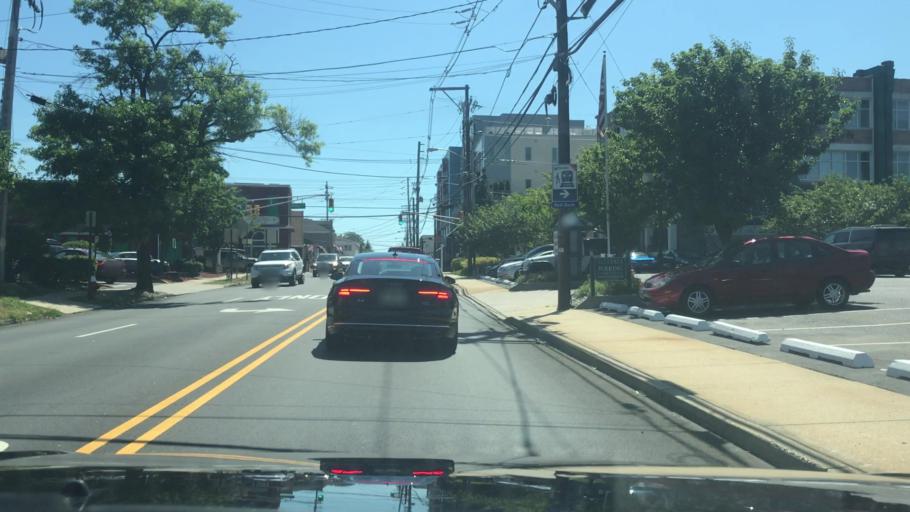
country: US
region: New Jersey
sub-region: Monmouth County
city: Red Bank
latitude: 40.3509
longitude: -74.0762
